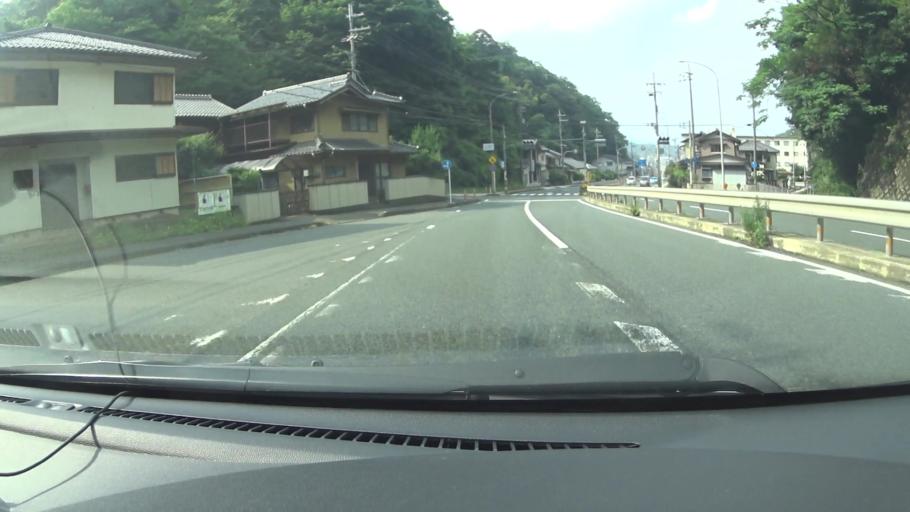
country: JP
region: Kyoto
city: Maizuru
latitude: 35.4651
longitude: 135.3634
